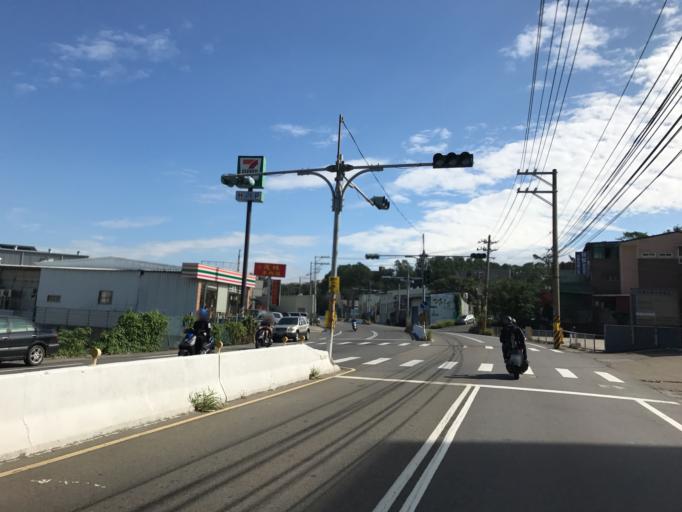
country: TW
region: Taiwan
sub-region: Hsinchu
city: Zhubei
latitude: 24.7768
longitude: 121.0368
